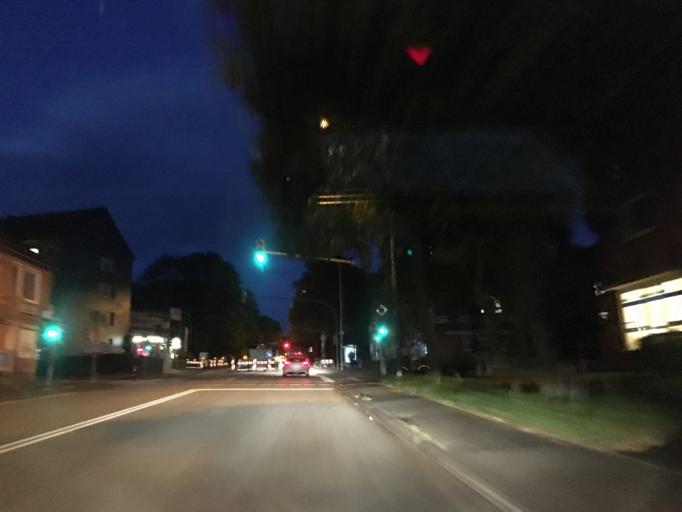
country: DE
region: Schleswig-Holstein
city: Kiel
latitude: 54.3074
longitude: 10.1415
